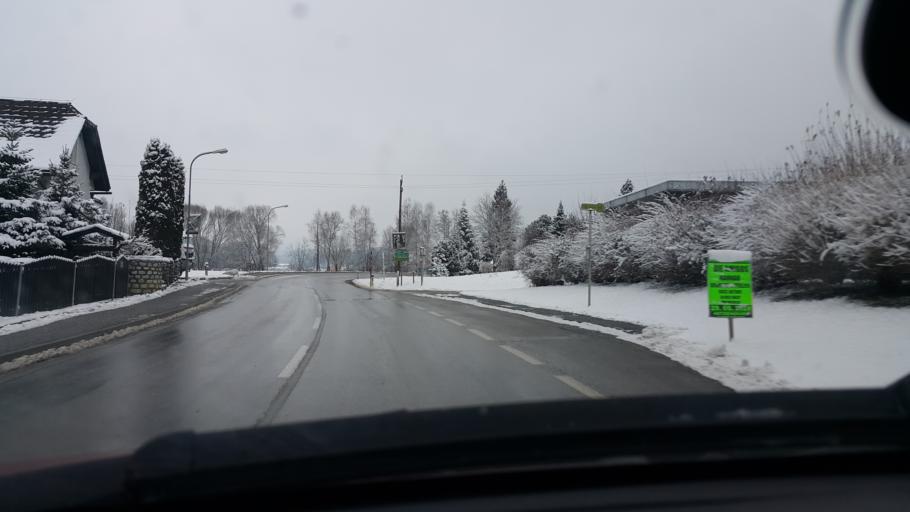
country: AT
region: Styria
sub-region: Politischer Bezirk Graz-Umgebung
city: Hitzendorf
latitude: 47.0436
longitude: 15.2925
